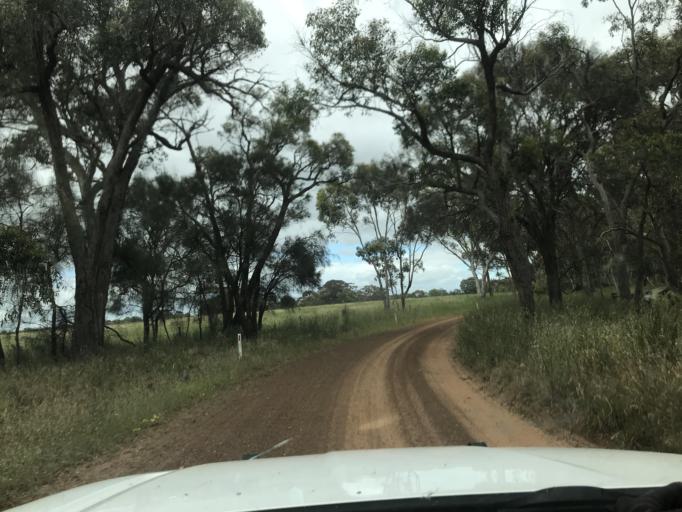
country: AU
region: South Australia
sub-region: Wattle Range
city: Penola
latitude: -37.1028
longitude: 141.2417
